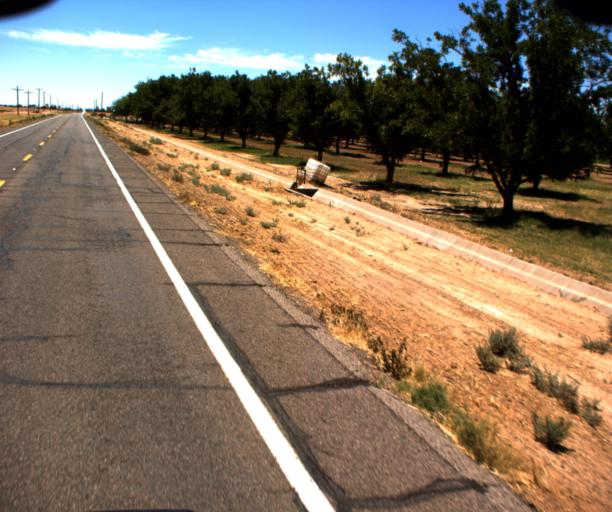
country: US
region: Arizona
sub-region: Pinal County
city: Coolidge
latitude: 32.8795
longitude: -111.5466
